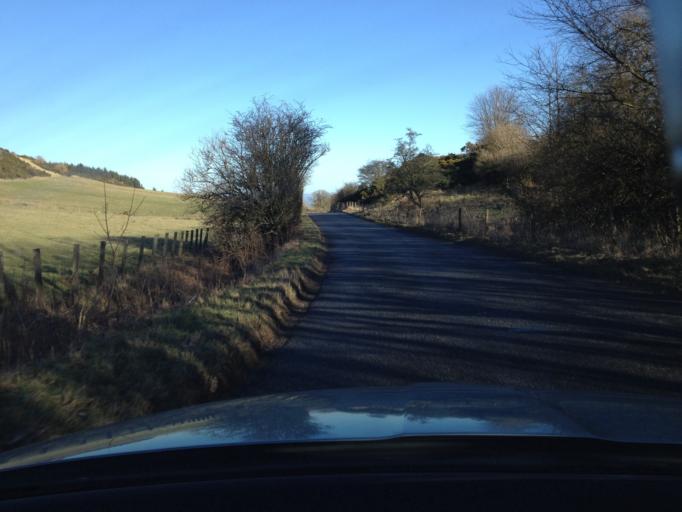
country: GB
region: Scotland
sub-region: Perth and Kinross
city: Bridge of Earn
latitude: 56.3106
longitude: -3.3801
